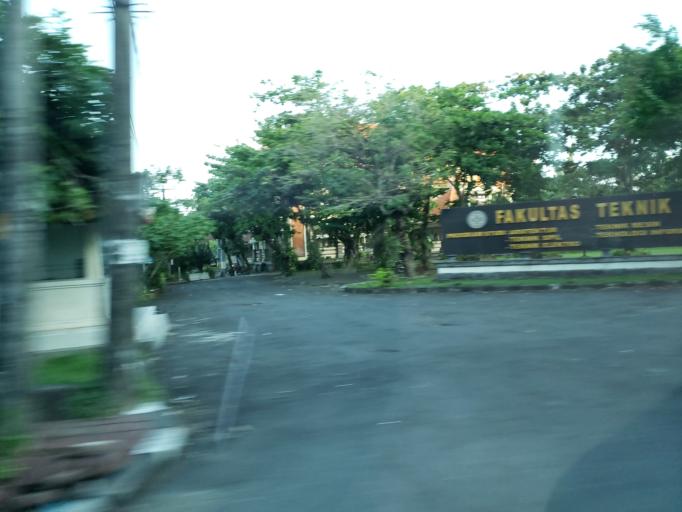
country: ID
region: Bali
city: Jimbaran
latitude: -8.7958
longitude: 115.1756
